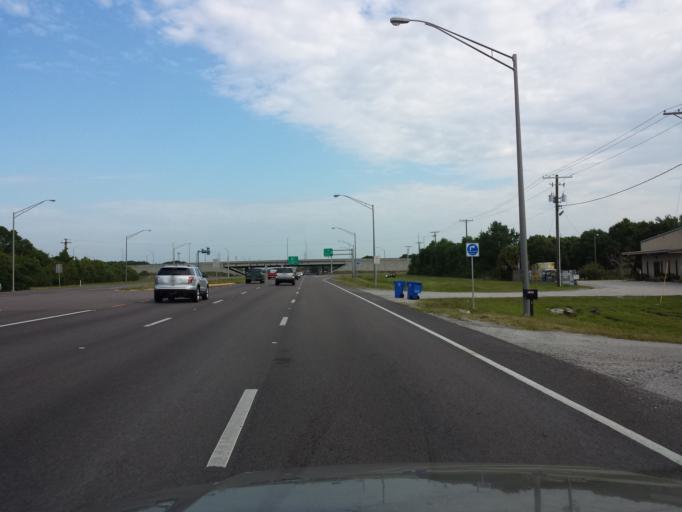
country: US
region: Florida
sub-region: Hillsborough County
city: Palm River-Clair Mel
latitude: 27.9270
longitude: -82.3505
